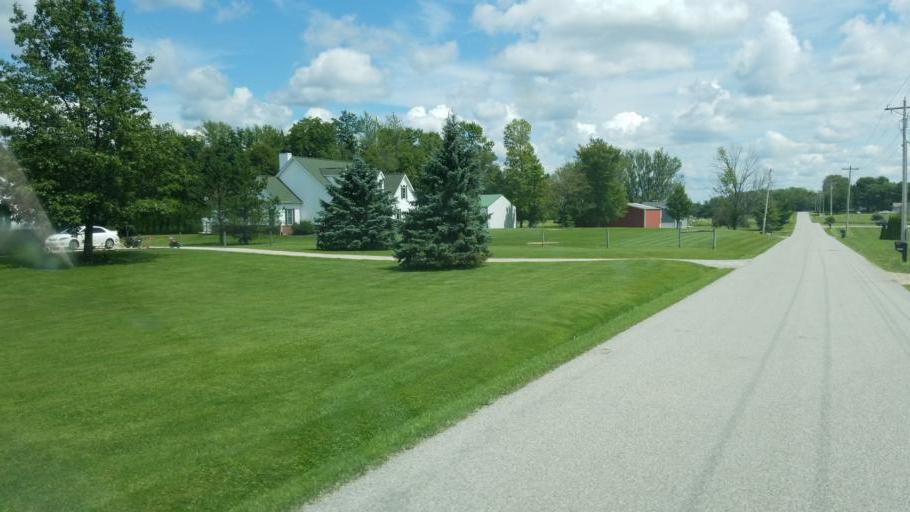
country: US
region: Ohio
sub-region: Knox County
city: Centerburg
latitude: 40.3725
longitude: -82.7058
